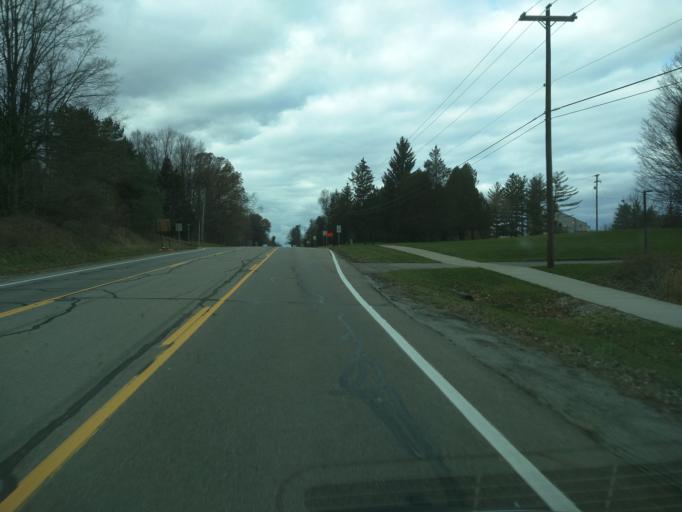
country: US
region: Michigan
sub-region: Ingham County
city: Haslett
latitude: 42.7133
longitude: -84.3846
